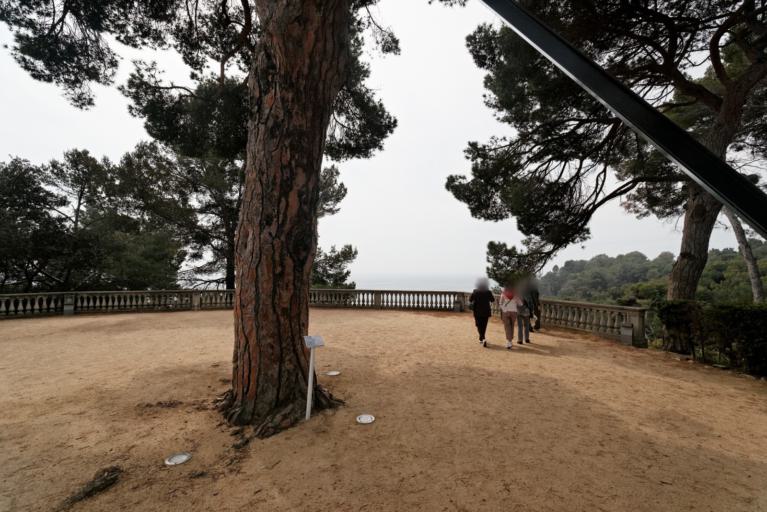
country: ES
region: Catalonia
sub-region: Provincia de Girona
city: Blanes
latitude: 41.6874
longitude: 2.8165
